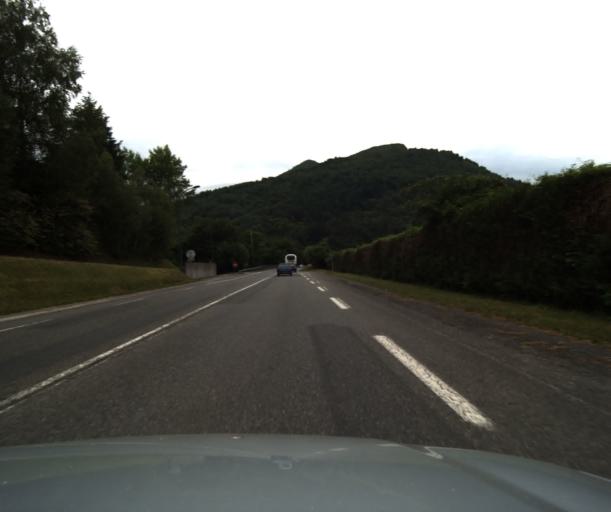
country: FR
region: Midi-Pyrenees
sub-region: Departement des Hautes-Pyrenees
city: Lourdes
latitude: 43.0986
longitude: -0.0298
